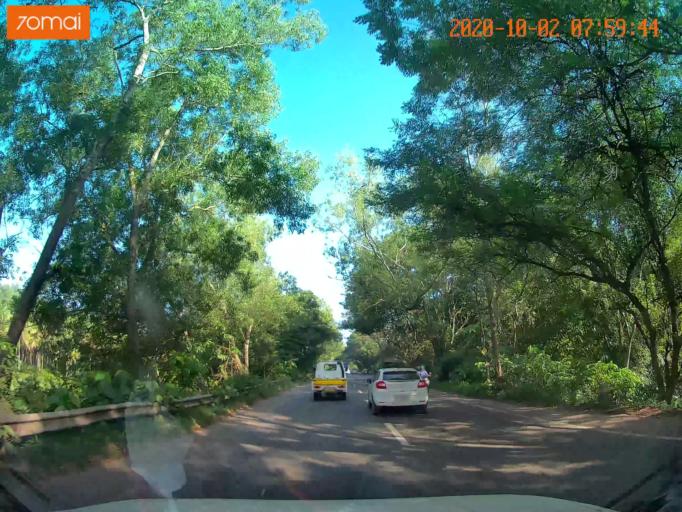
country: IN
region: Kerala
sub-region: Kozhikode
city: Ferokh
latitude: 11.2124
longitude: 75.8601
